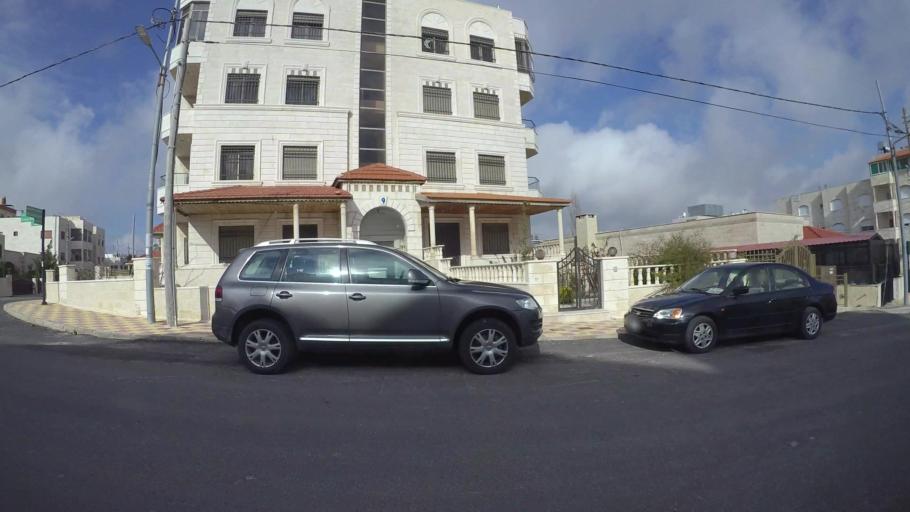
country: JO
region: Amman
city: Al Jubayhah
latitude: 32.0405
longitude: 35.8698
